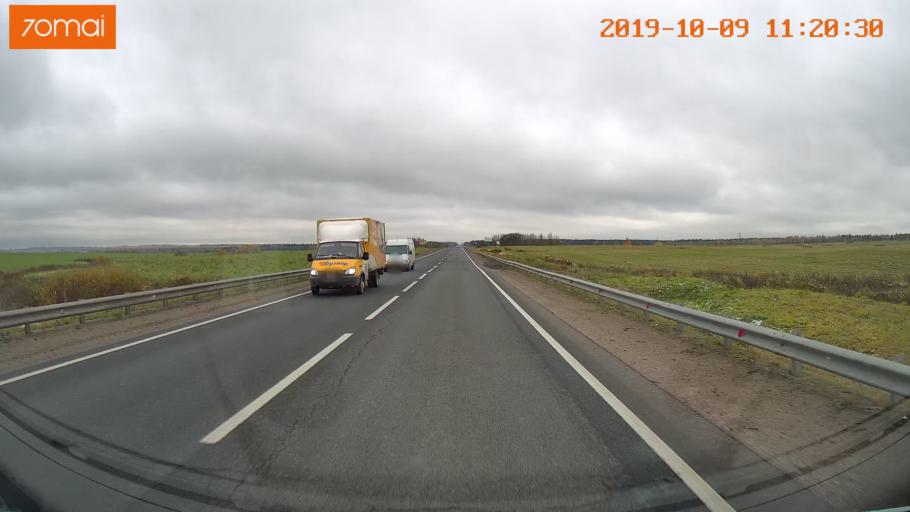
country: RU
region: Vologda
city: Vologda
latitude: 59.1491
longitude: 39.9390
